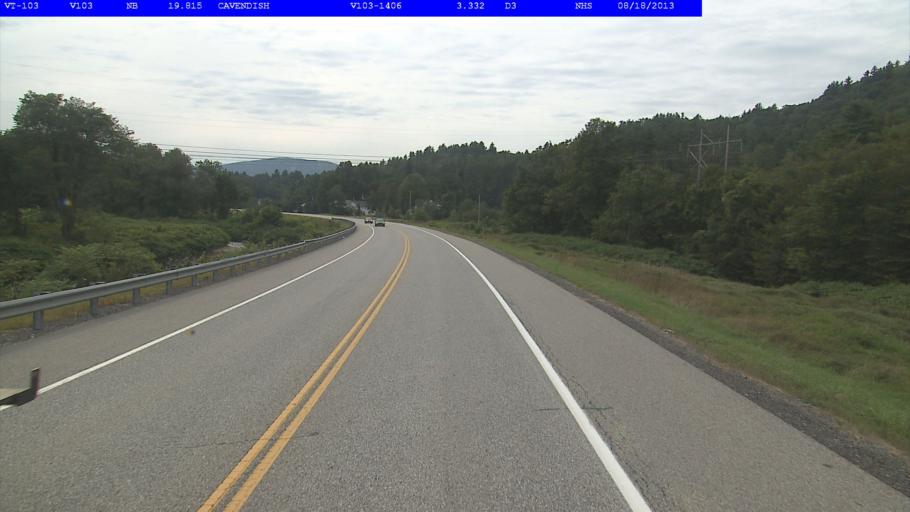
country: US
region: Vermont
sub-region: Windsor County
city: Chester
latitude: 43.3879
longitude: -72.6538
